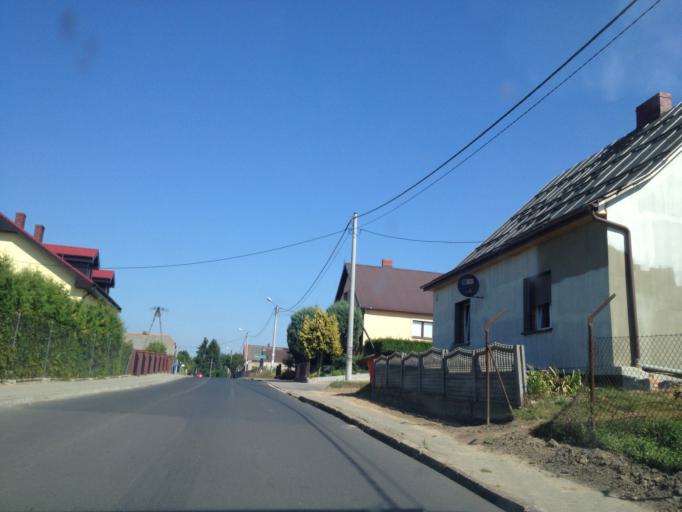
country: PL
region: Greater Poland Voivodeship
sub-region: Powiat sredzki
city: Zaniemysl
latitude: 52.1168
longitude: 17.1165
